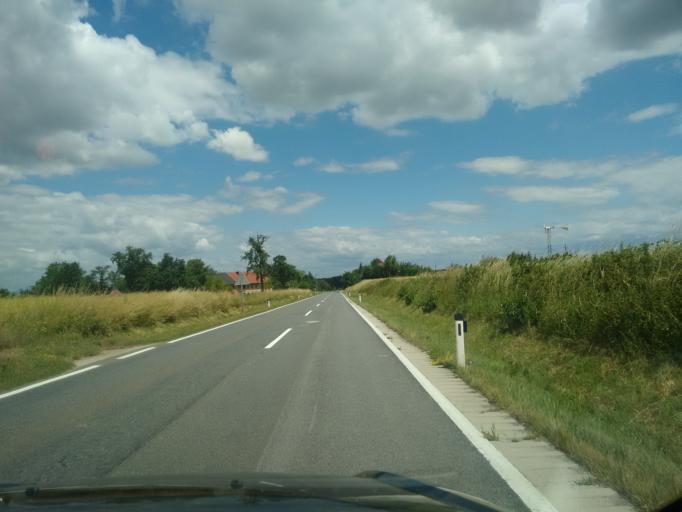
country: AT
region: Upper Austria
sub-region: Politischer Bezirk Steyr-Land
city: Sierning
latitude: 48.1025
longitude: 14.3180
